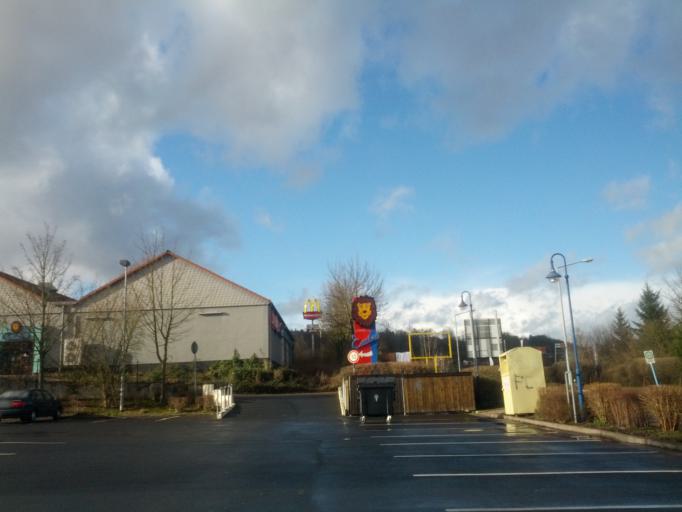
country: DE
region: Thuringia
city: Eisenach
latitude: 50.9926
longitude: 10.2939
